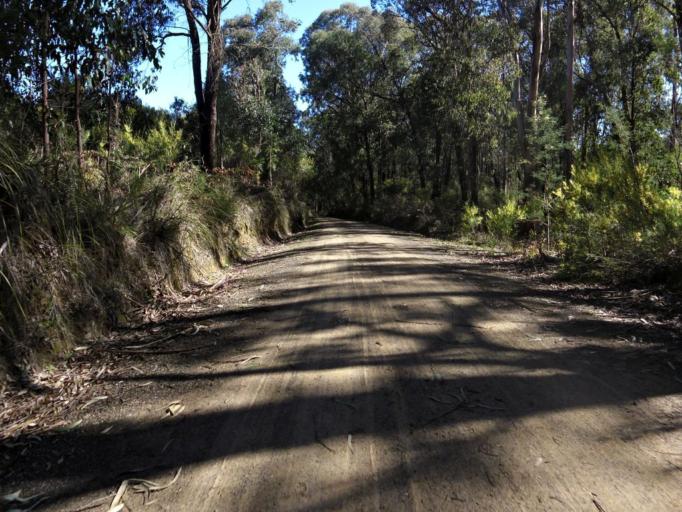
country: AU
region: Victoria
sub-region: Latrobe
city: Moe
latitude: -38.3709
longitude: 146.2041
